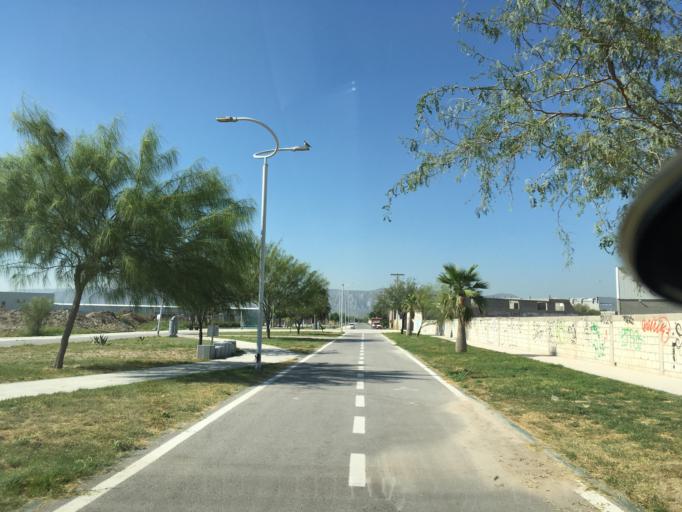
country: MX
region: Coahuila
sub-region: Torreon
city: Fraccionamiento la Noria
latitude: 25.5268
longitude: -103.3758
